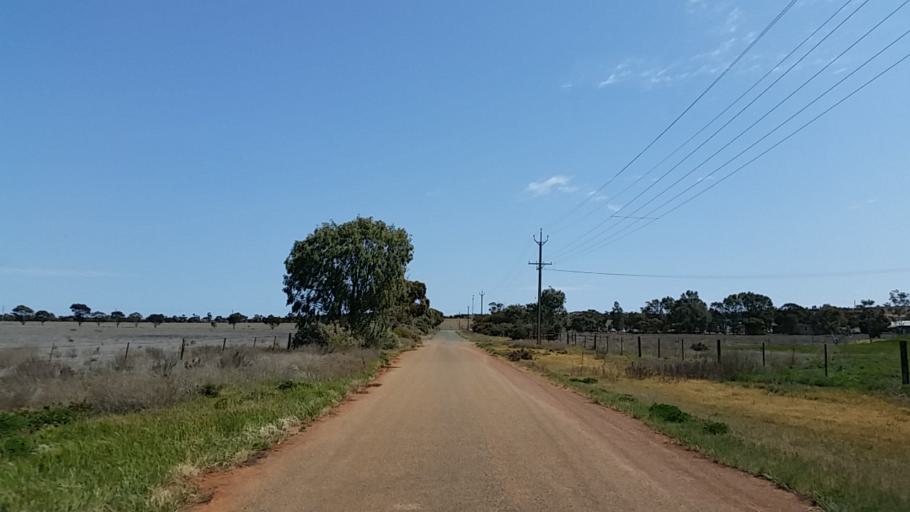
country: AU
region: South Australia
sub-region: Peterborough
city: Peterborough
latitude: -32.9595
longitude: 138.8506
